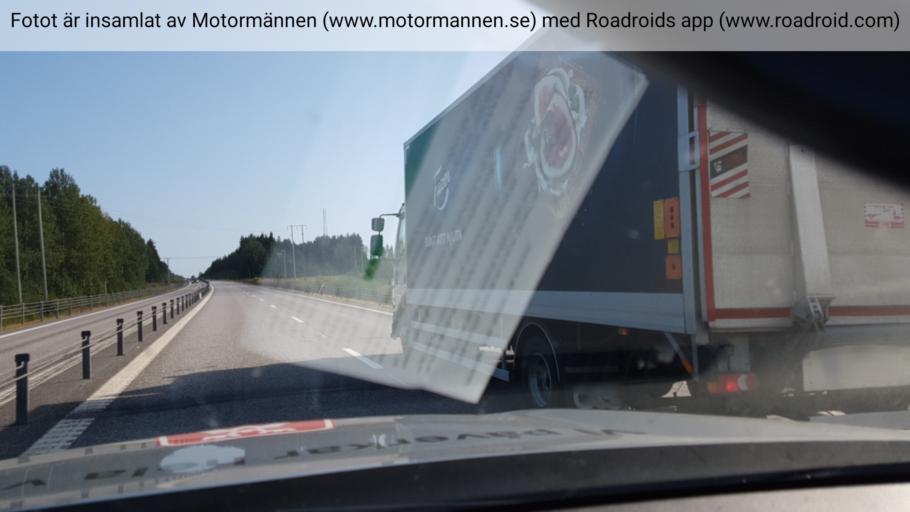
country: SE
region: Norrbotten
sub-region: Pitea Kommun
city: Pitea
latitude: 65.2545
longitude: 21.4734
